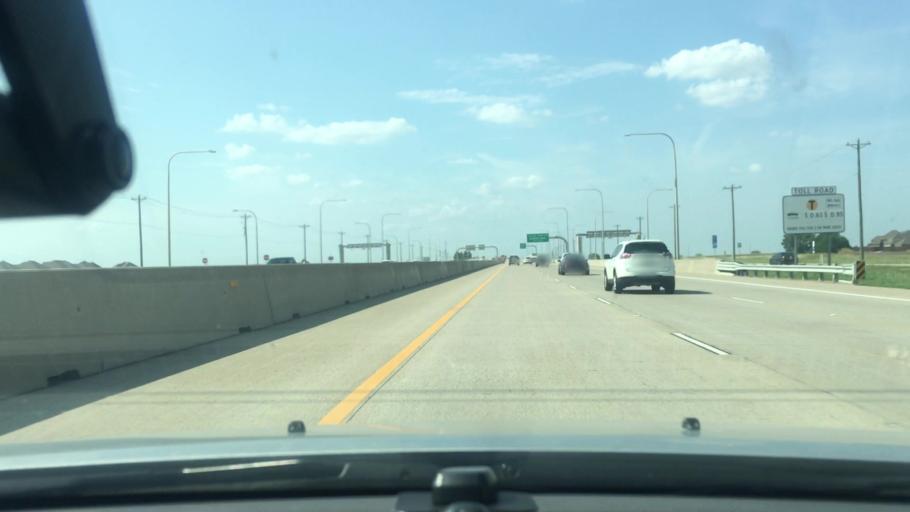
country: US
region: Texas
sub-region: Collin County
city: Frisco
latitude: 33.1828
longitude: -96.8392
